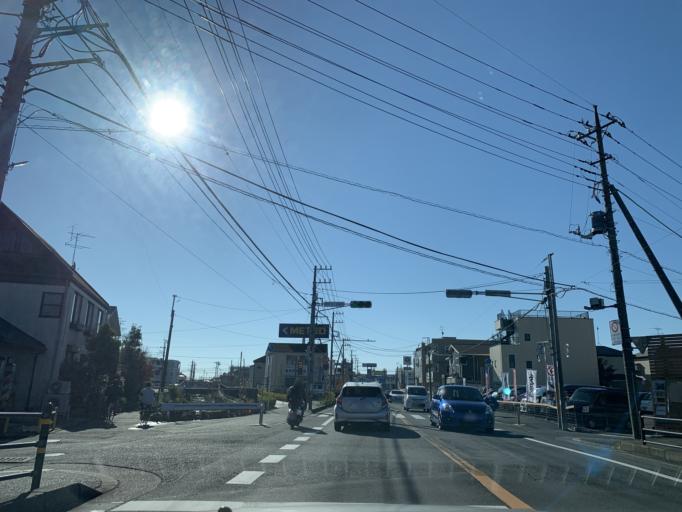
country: JP
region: Chiba
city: Nagareyama
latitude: 35.8472
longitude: 139.8979
